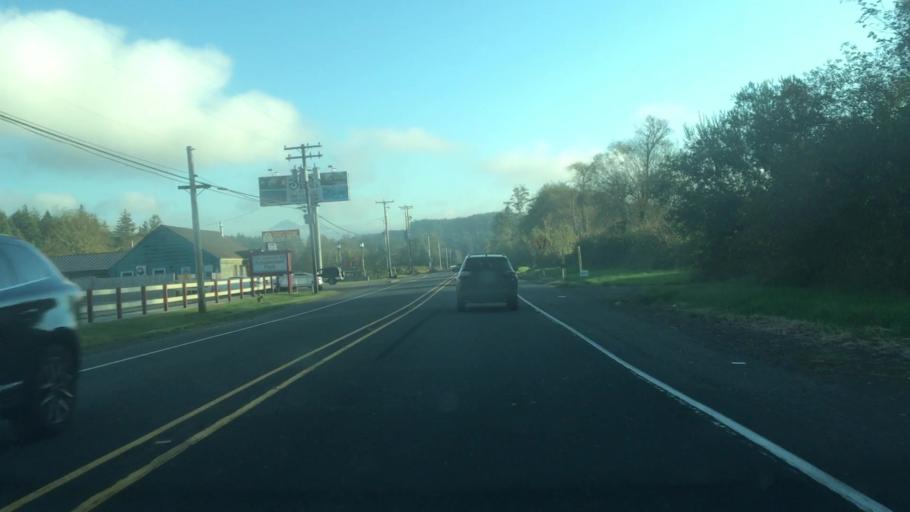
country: US
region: Oregon
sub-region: Clatsop County
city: Seaside
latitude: 45.9721
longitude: -123.9262
